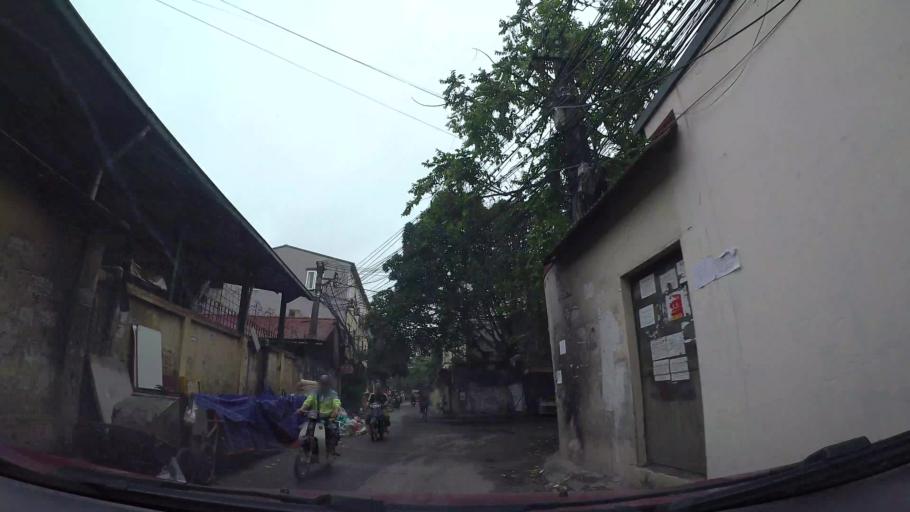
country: VN
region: Ha Noi
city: Dong Da
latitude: 21.0064
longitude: 105.8282
